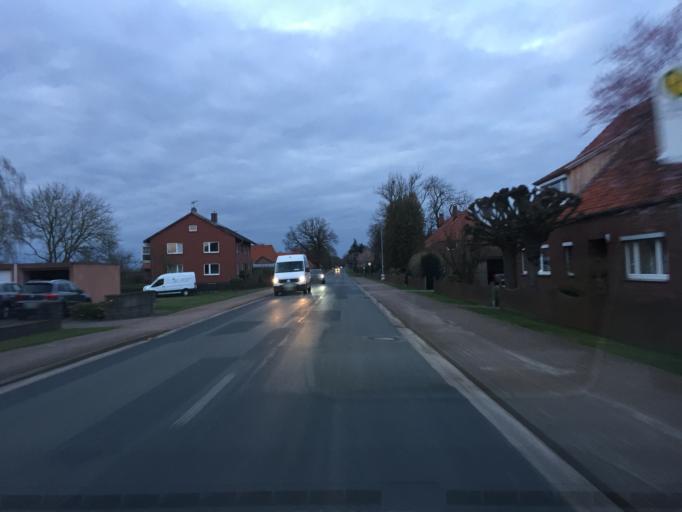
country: DE
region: Lower Saxony
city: Steimbke
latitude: 52.6295
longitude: 9.3894
